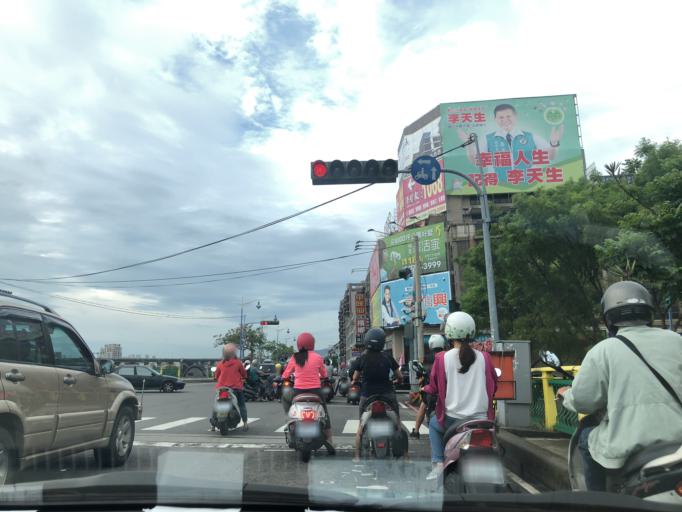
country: TW
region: Taiwan
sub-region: Taichung City
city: Taichung
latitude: 24.0995
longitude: 120.6940
